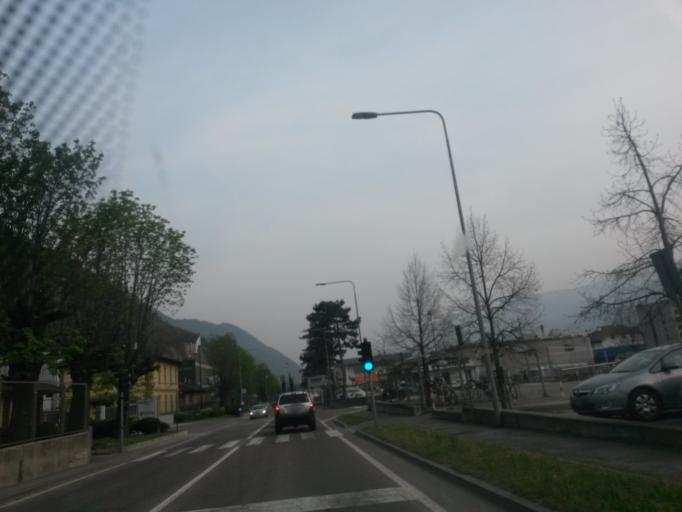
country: IT
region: Trentino-Alto Adige
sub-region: Bolzano
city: Sinigo
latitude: 46.6349
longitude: 11.1770
